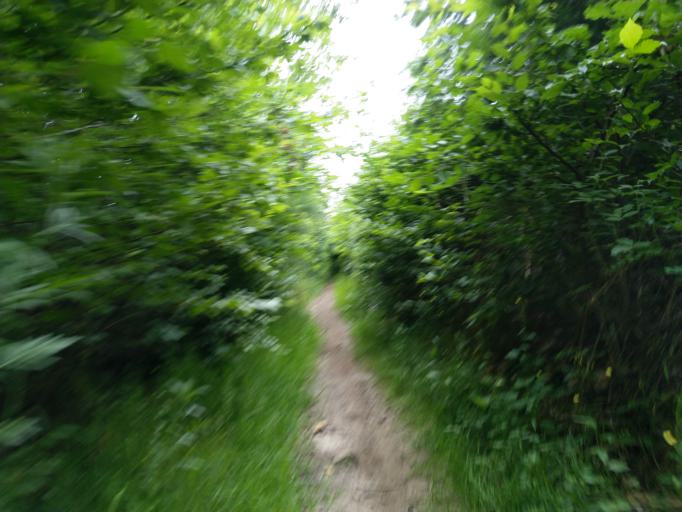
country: BE
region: Wallonia
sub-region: Province du Hainaut
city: Jurbise
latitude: 50.4974
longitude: 3.8792
